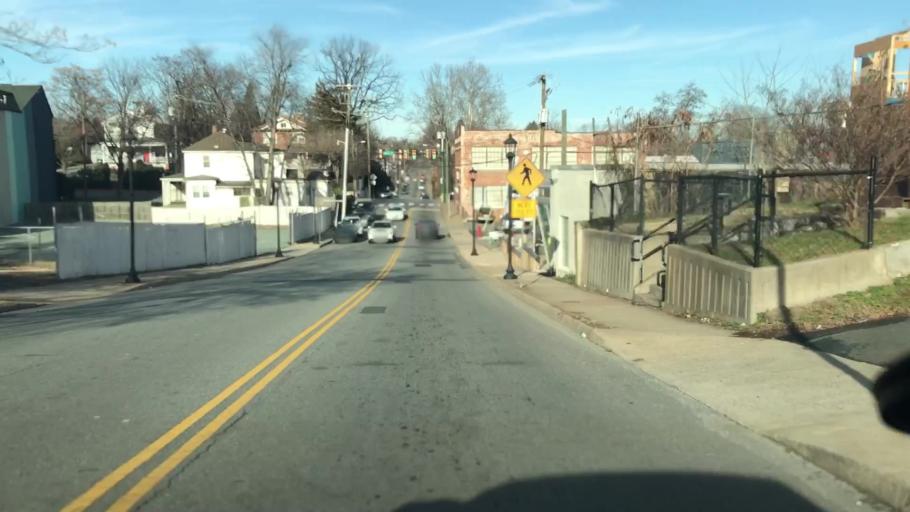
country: US
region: Virginia
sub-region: City of Charlottesville
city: Charlottesville
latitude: 38.0331
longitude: -78.4945
